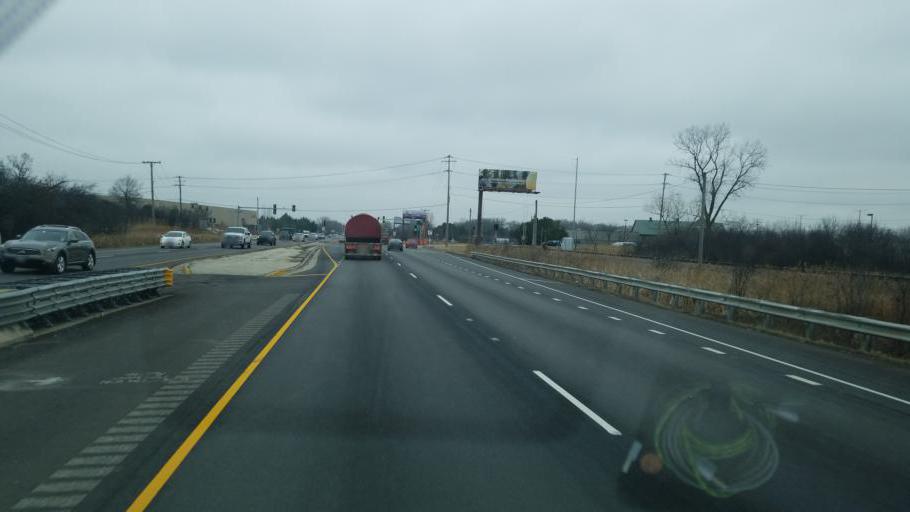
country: US
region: Illinois
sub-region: Lake County
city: Park City
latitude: 42.3181
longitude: -87.8797
